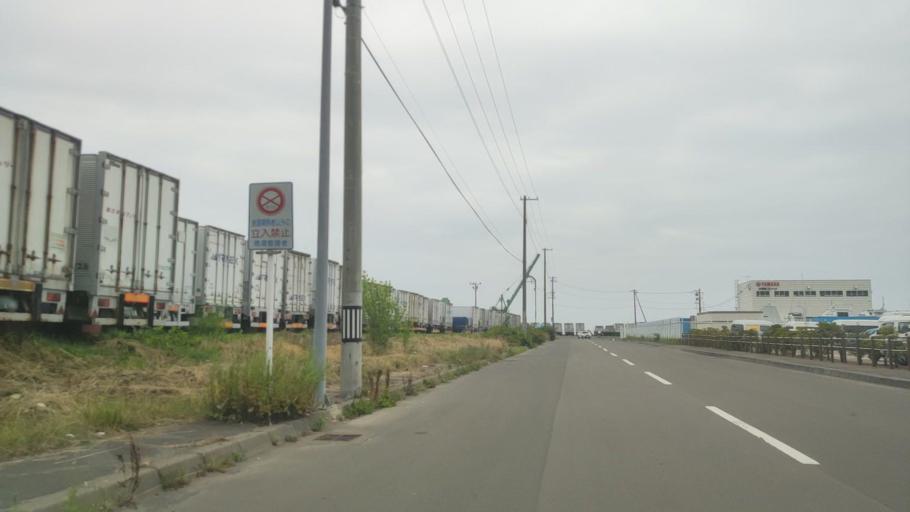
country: JP
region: Hokkaido
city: Otaru
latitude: 43.1866
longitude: 141.0226
